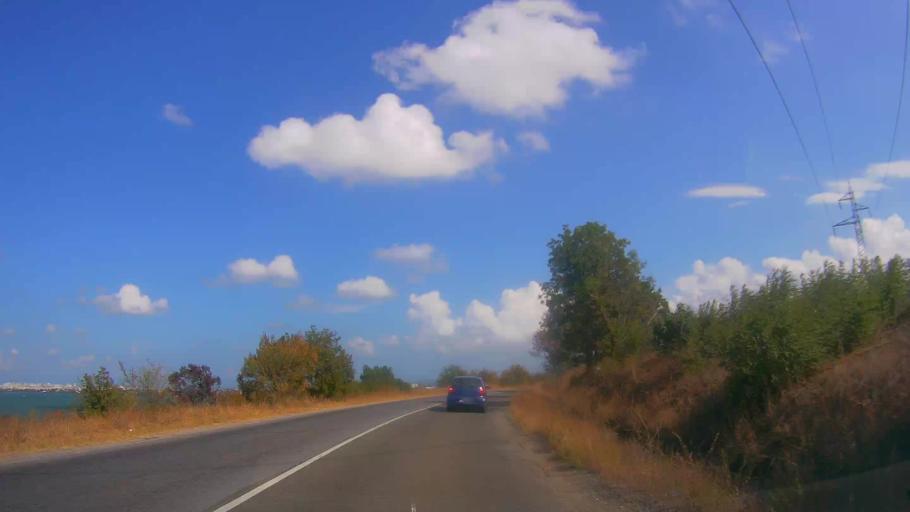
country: BG
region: Burgas
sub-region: Obshtina Burgas
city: Burgas
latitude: 42.4775
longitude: 27.4134
